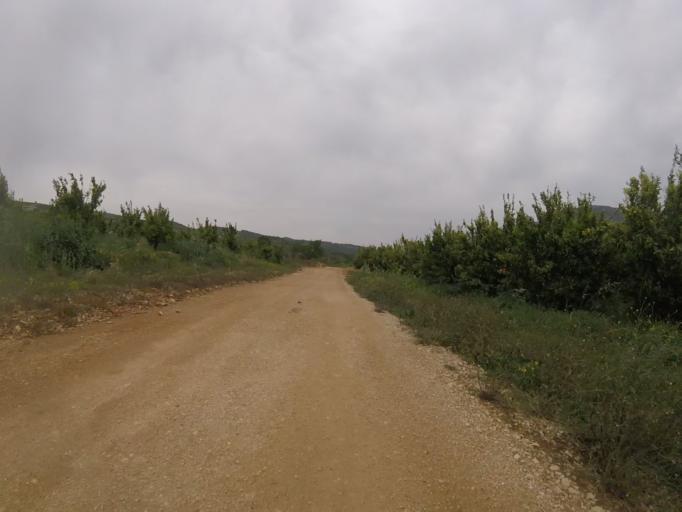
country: ES
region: Valencia
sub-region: Provincia de Castello
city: Alcala de Xivert
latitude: 40.2852
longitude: 0.2571
